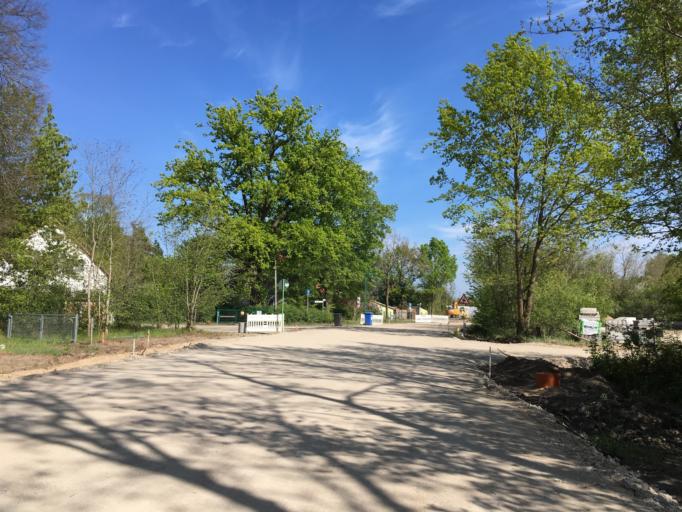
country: DE
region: Brandenburg
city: Rudnitz
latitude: 52.7248
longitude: 13.6135
